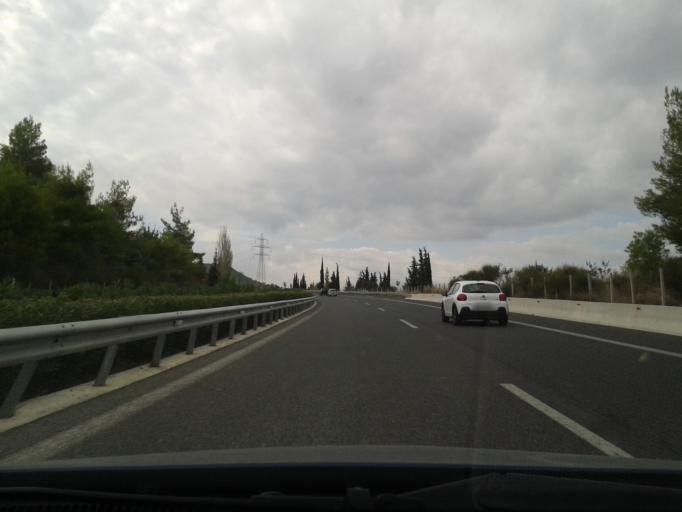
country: GR
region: Peloponnese
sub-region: Nomos Korinthias
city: Arkhaia Korinthos
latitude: 37.8735
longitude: 22.8654
